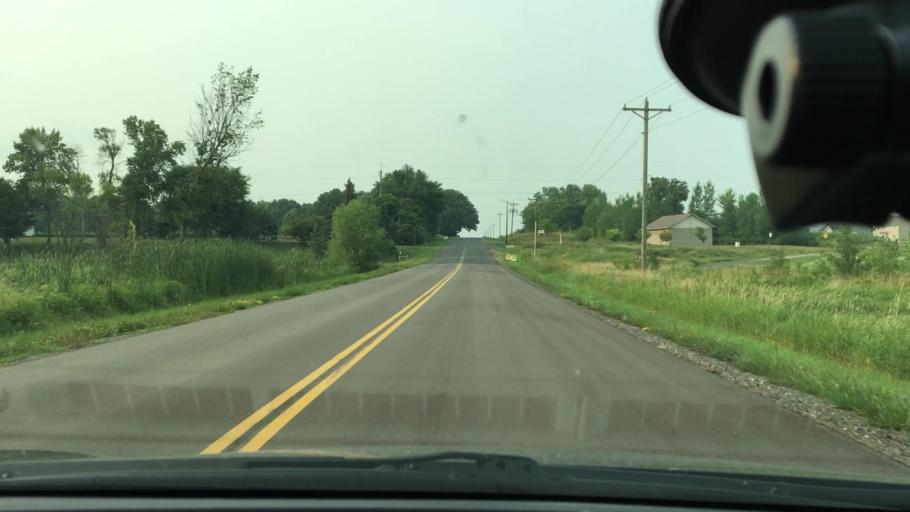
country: US
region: Minnesota
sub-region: Wright County
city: Albertville
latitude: 45.2795
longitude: -93.6840
